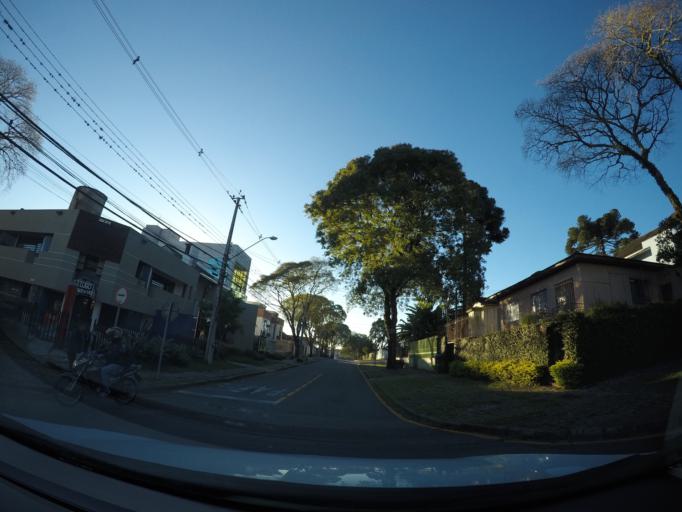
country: BR
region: Parana
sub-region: Curitiba
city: Curitiba
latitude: -25.4178
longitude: -49.2792
